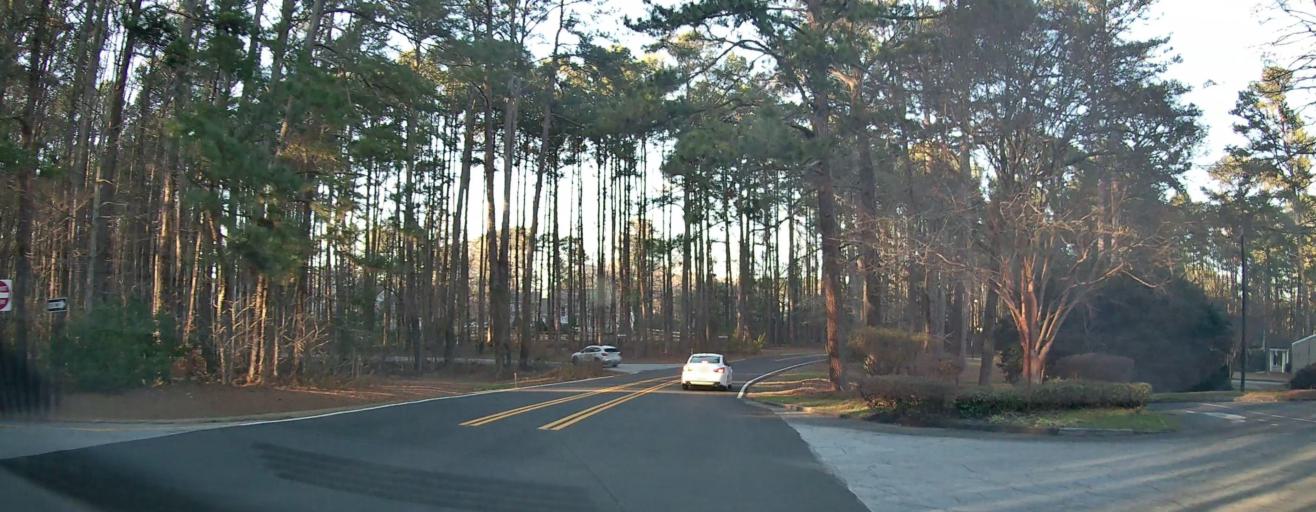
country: US
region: Georgia
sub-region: Fayette County
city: Peachtree City
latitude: 33.4014
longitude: -84.5872
